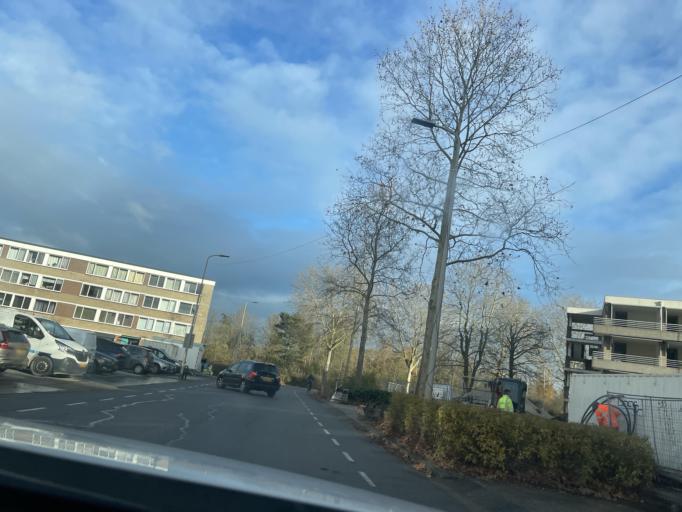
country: NL
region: South Holland
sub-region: Gemeente Capelle aan den IJssel
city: Capelle aan den IJssel
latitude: 51.9343
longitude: 4.5932
